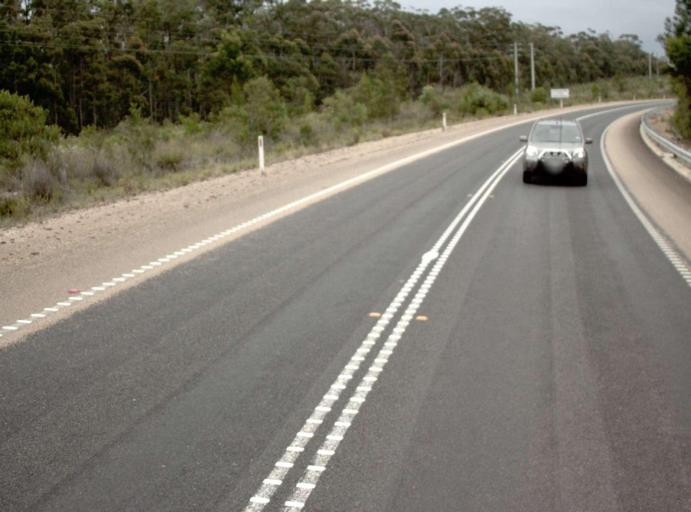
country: AU
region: Victoria
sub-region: East Gippsland
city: Lakes Entrance
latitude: -37.7019
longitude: 148.0513
